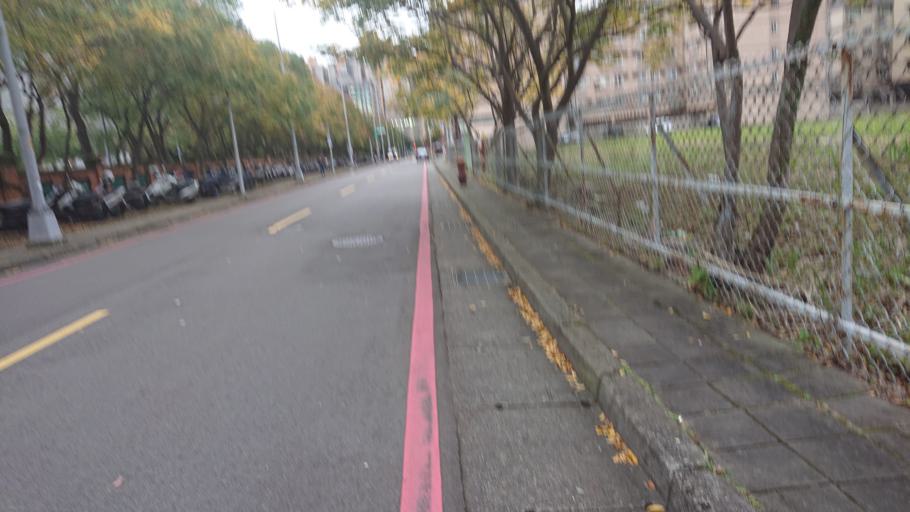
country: TW
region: Taiwan
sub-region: Taoyuan
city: Taoyuan
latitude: 24.9425
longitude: 121.3713
